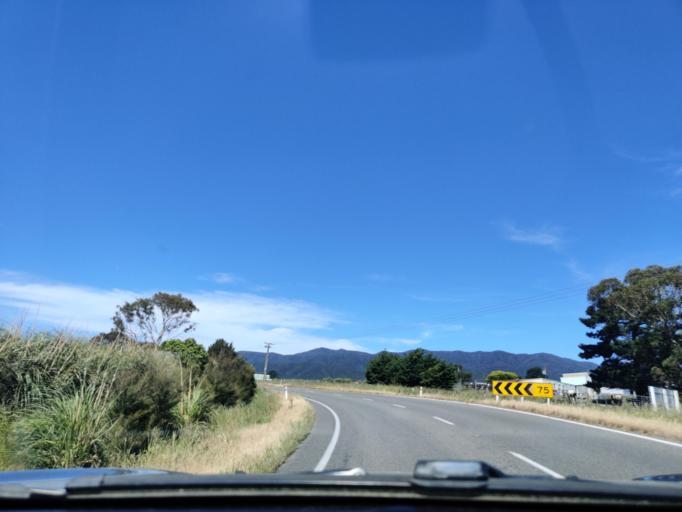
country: NZ
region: Wellington
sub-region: Upper Hutt City
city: Upper Hutt
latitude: -41.3295
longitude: 175.2339
